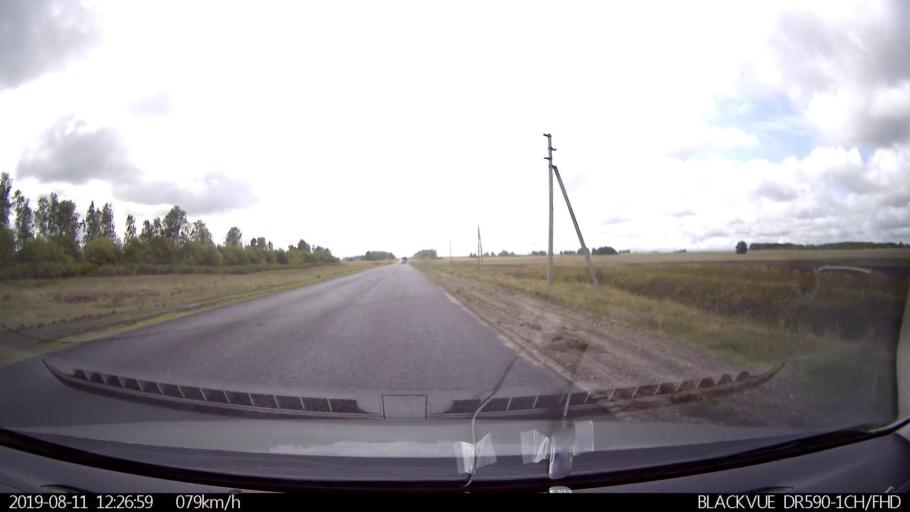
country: RU
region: Ulyanovsk
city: Ignatovka
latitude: 53.8592
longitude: 47.9261
